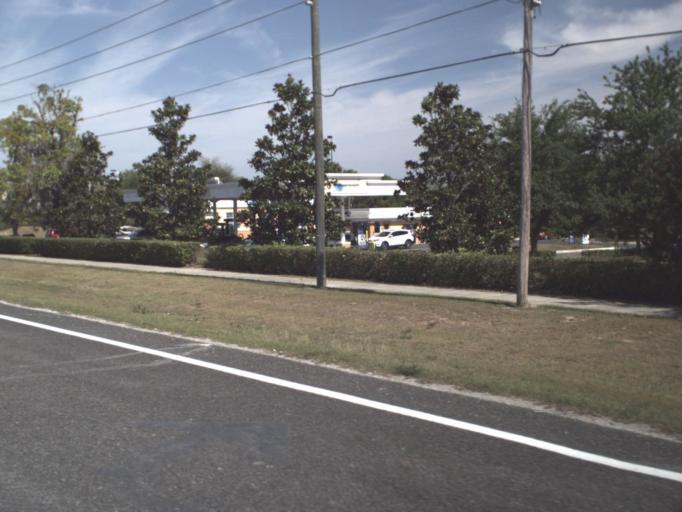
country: US
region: Florida
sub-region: Lake County
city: Lady Lake
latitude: 28.9321
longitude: -81.9321
